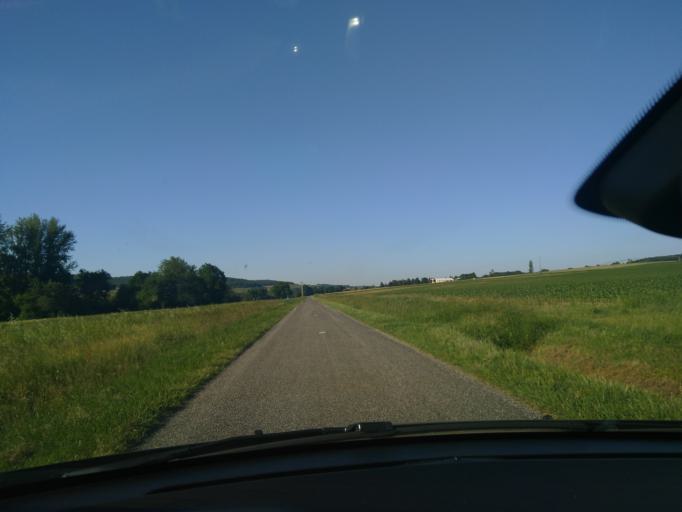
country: FR
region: Midi-Pyrenees
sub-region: Departement du Tarn-et-Garonne
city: Beaumont-de-Lomagne
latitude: 43.8401
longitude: 1.0724
